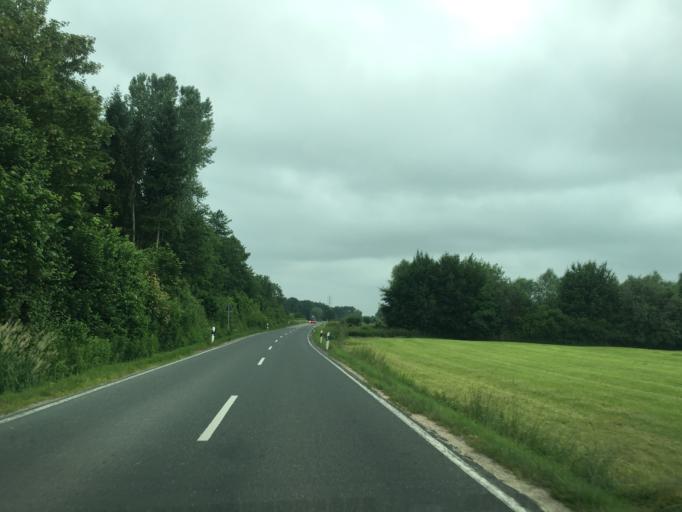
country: DE
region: North Rhine-Westphalia
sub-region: Regierungsbezirk Munster
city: Laer
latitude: 52.0674
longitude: 7.3521
